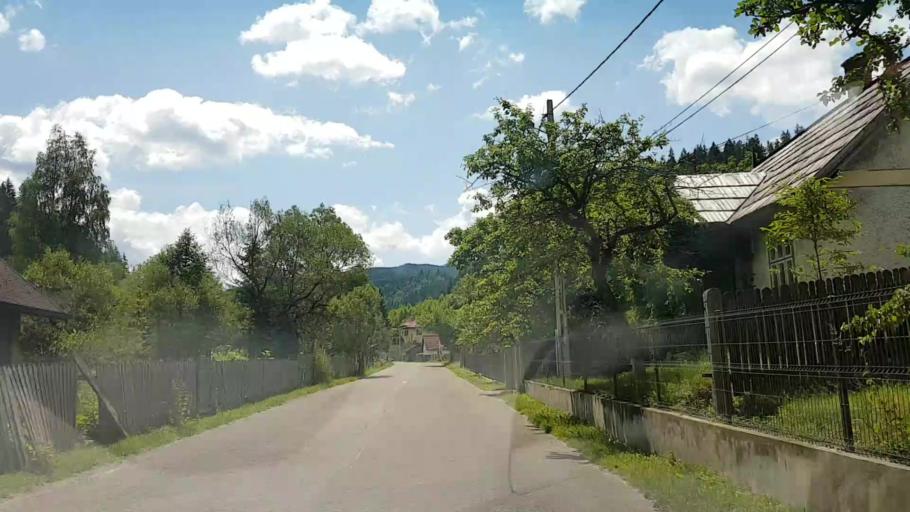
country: RO
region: Suceava
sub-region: Comuna Pojorata
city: Pojorata
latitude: 47.4908
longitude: 25.4859
